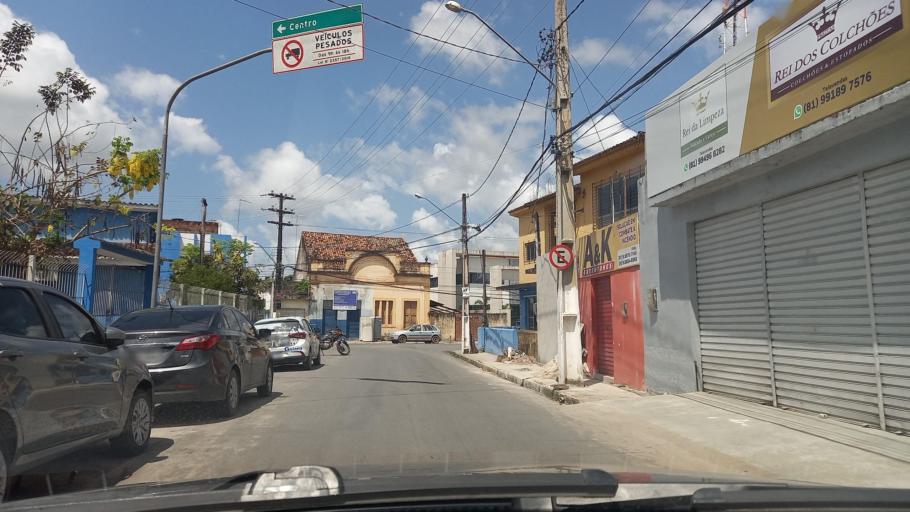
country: BR
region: Pernambuco
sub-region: Goiana
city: Goiana
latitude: -7.5637
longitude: -34.9999
